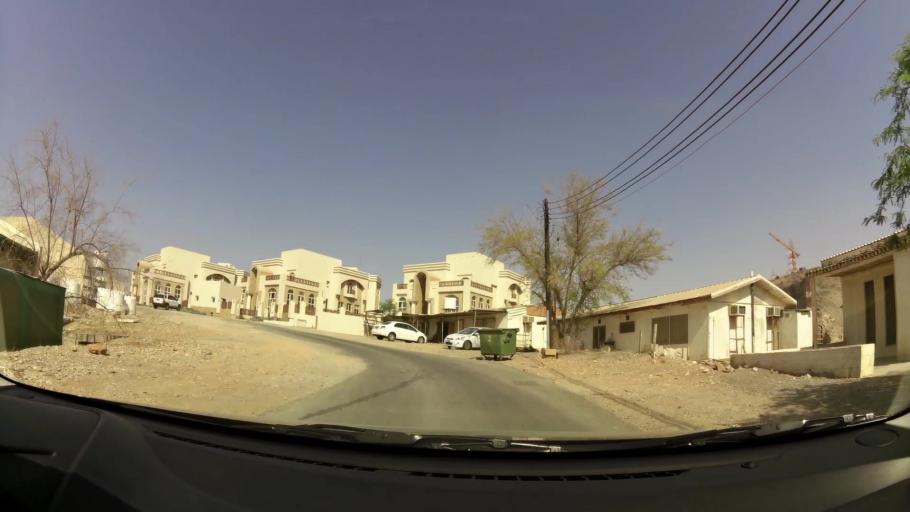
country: OM
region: Muhafazat Masqat
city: Muscat
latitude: 23.6027
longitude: 58.4954
